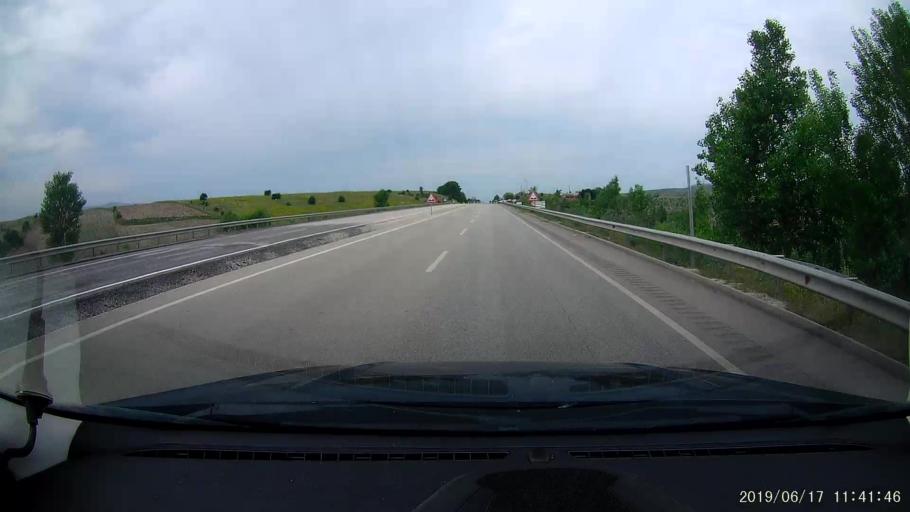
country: TR
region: Cankiri
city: Kursunlu
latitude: 40.8322
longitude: 33.3172
